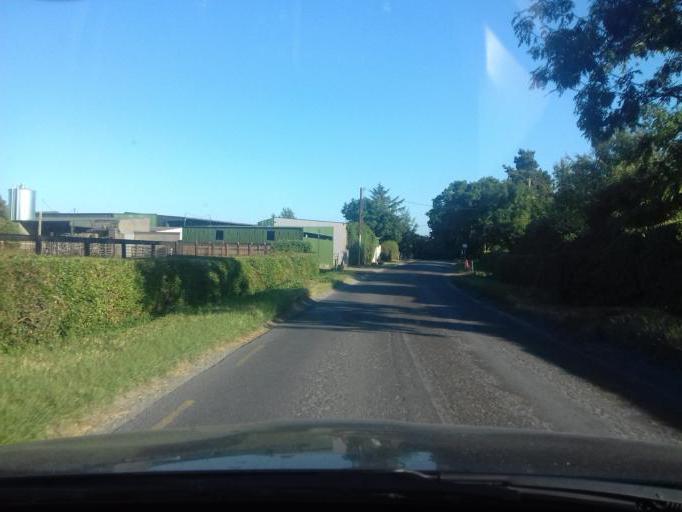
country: IE
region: Leinster
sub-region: Dublin City
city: Finglas
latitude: 53.4467
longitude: -6.3054
